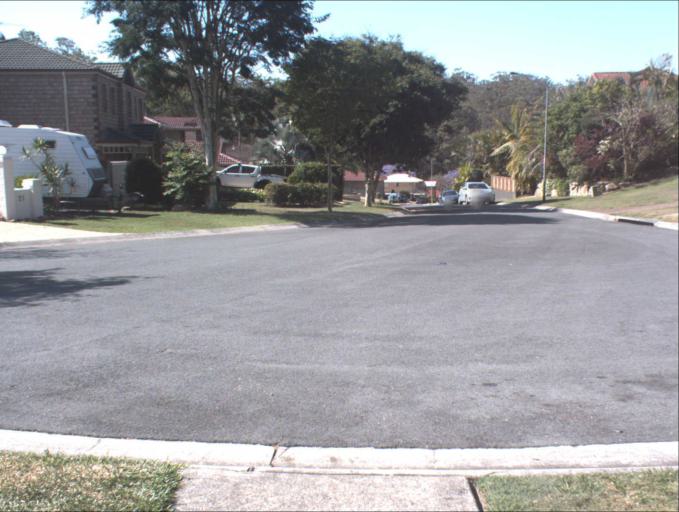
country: AU
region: Queensland
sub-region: Logan
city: Slacks Creek
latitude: -27.6437
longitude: 153.1909
